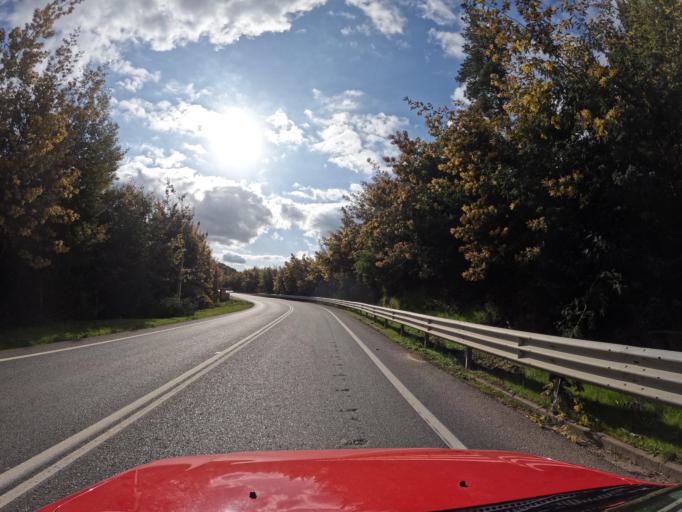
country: CL
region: Maule
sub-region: Provincia de Talca
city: Constitucion
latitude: -35.5426
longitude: -72.1532
